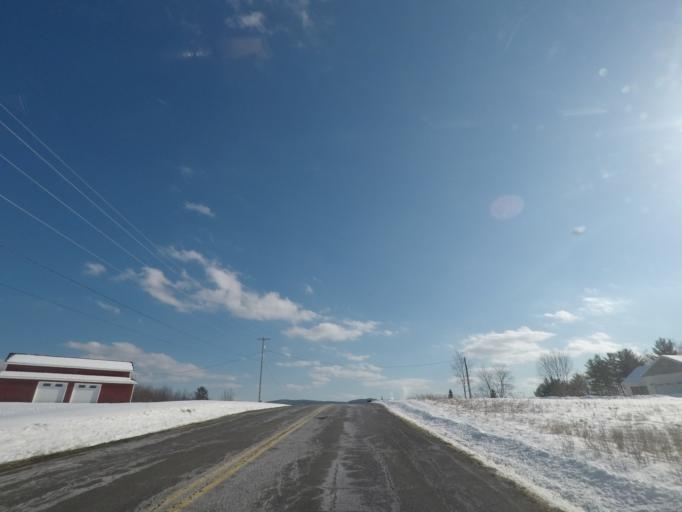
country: US
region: New York
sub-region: Rensselaer County
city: Hoosick Falls
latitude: 42.8450
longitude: -73.4891
